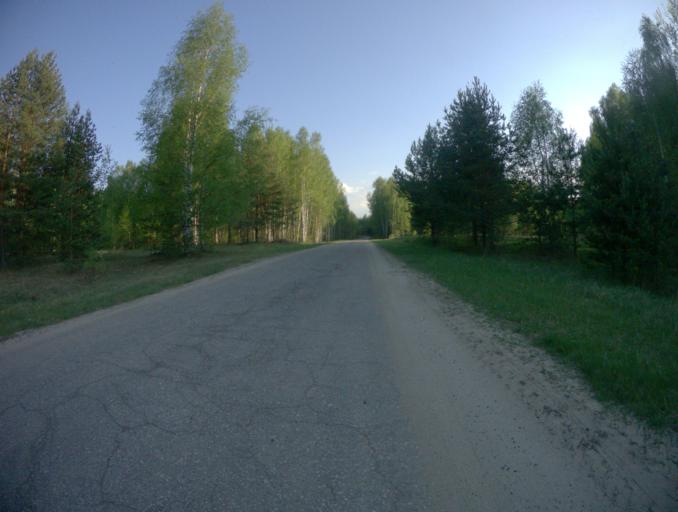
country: RU
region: Vladimir
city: Vyazniki
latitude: 56.3576
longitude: 42.1362
